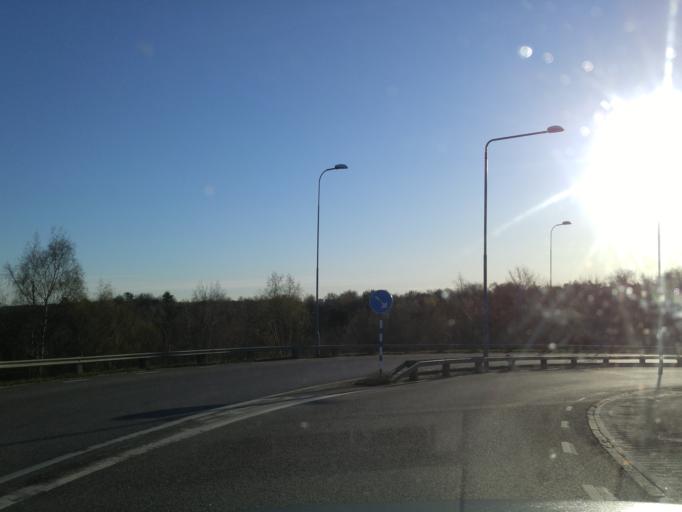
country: SE
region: Vaestra Goetaland
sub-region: Goteborg
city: Majorna
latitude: 57.6764
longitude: 11.9164
